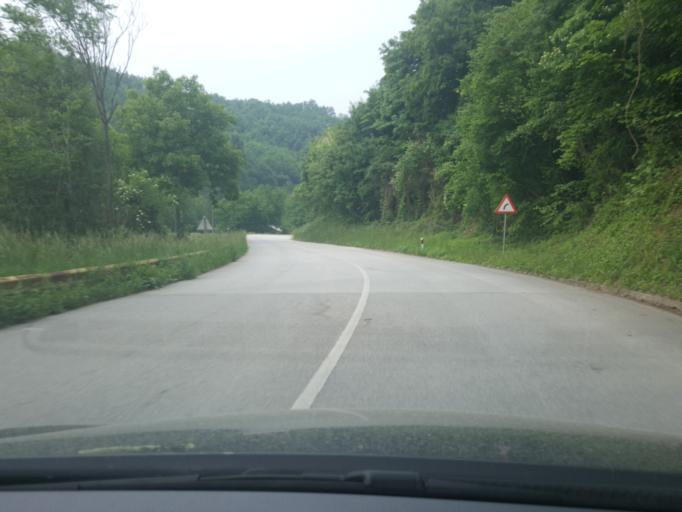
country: RS
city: Gornja Bukovica
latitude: 44.2588
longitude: 19.8164
